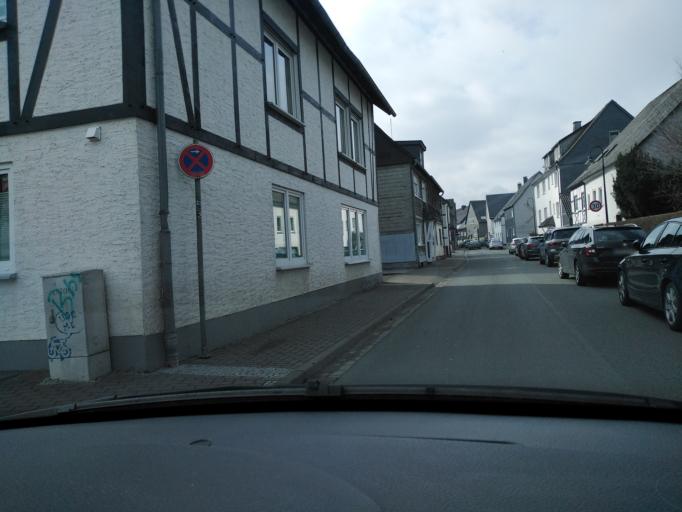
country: DE
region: North Rhine-Westphalia
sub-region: Regierungsbezirk Arnsberg
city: Brilon
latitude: 51.3974
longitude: 8.5664
